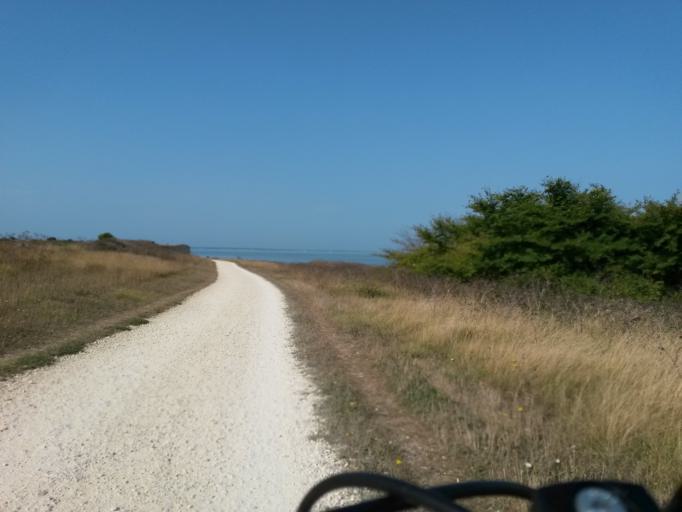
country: FR
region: Poitou-Charentes
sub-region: Departement de la Charente-Maritime
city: Nieul-sur-Mer
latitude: 46.2156
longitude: -1.1916
